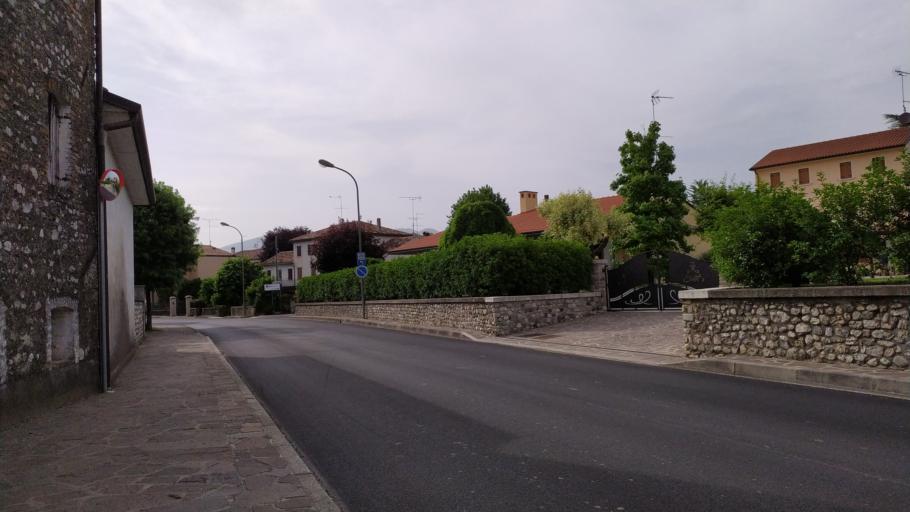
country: IT
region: Veneto
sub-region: Provincia di Treviso
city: Falze di Piave
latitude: 45.8603
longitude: 12.1695
